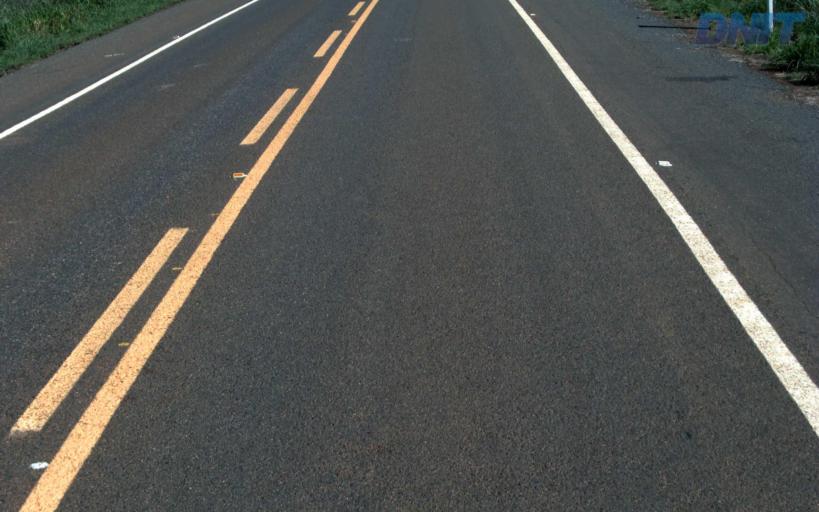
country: BR
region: Goias
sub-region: Sao Miguel Do Araguaia
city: Sao Miguel do Araguaia
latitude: -13.3497
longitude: -50.1497
